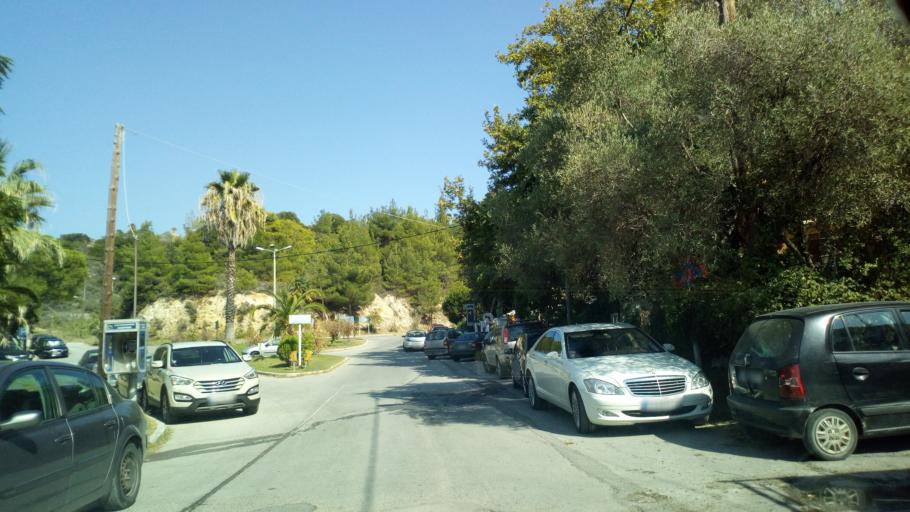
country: GR
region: Central Macedonia
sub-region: Nomos Chalkidikis
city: Stratonion
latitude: 40.5903
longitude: 23.7877
